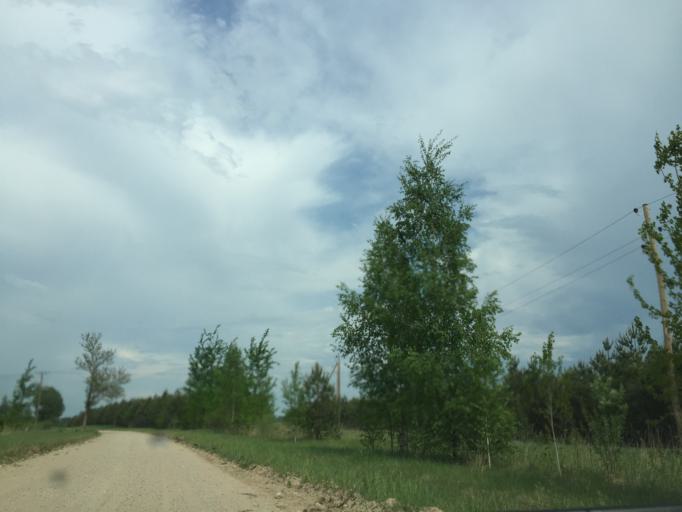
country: LV
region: Livani
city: Livani
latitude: 56.5752
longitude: 26.1705
